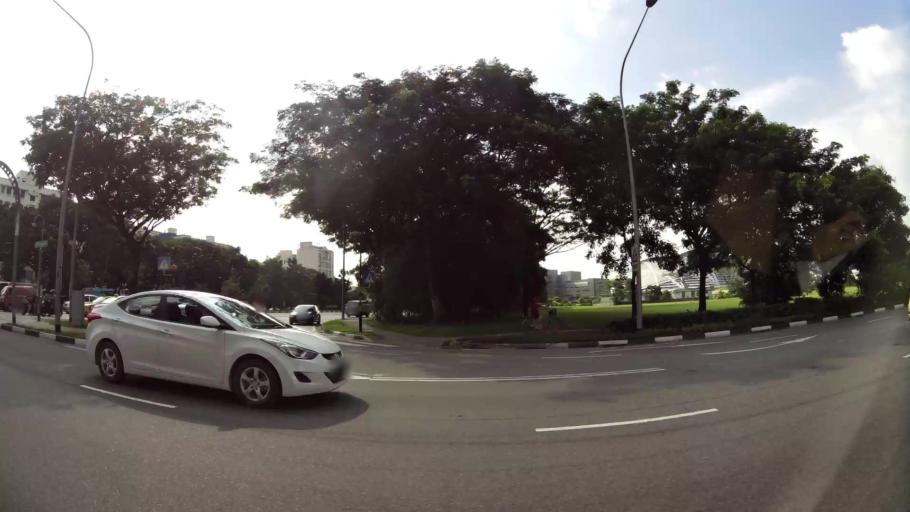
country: SG
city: Singapore
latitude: 1.3114
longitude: 103.8749
